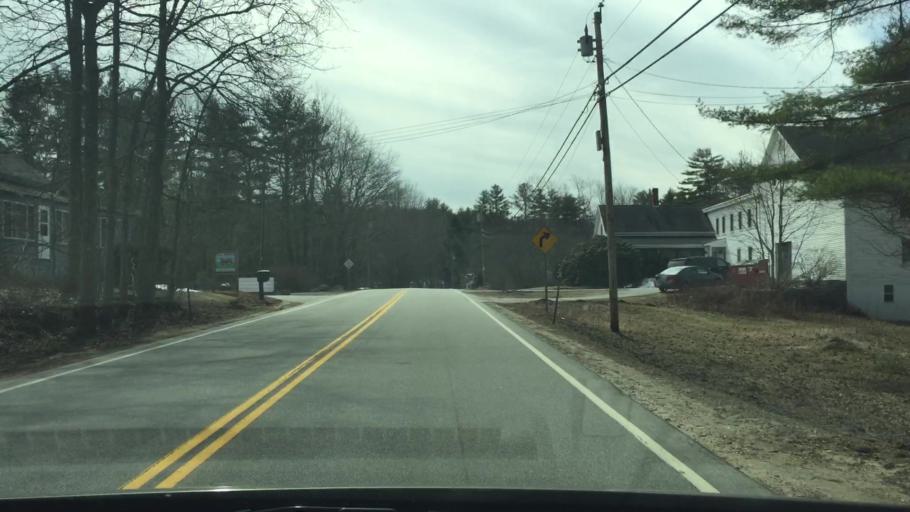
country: US
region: New Hampshire
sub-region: Strafford County
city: Barrington
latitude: 43.2375
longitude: -71.0556
